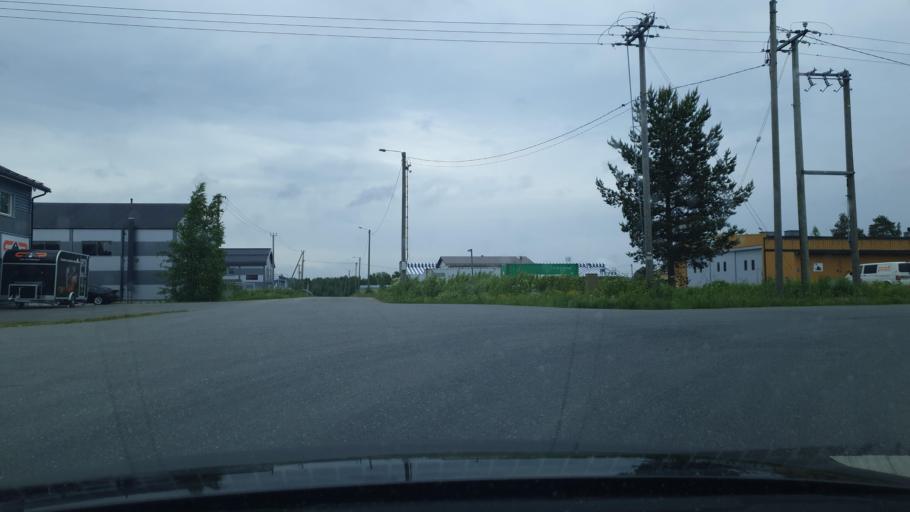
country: FI
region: Northern Ostrobothnia
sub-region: Oulunkaari
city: Ii
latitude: 65.3088
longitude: 25.3773
